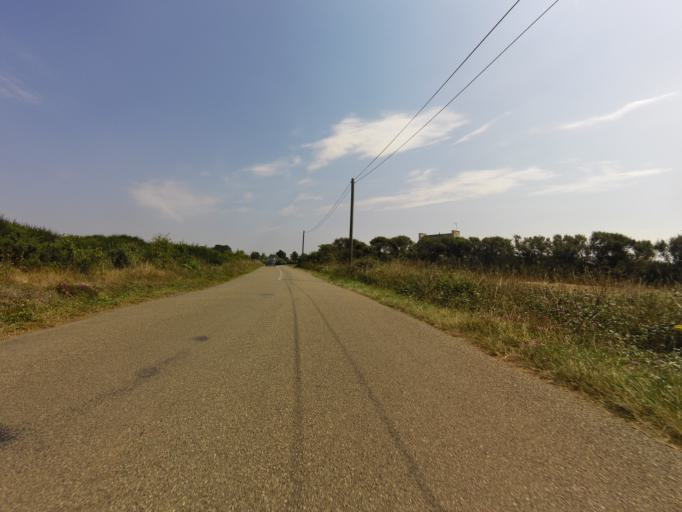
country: FR
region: Brittany
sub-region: Departement du Finistere
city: Pouldreuzic
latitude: 47.9103
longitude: -4.3411
